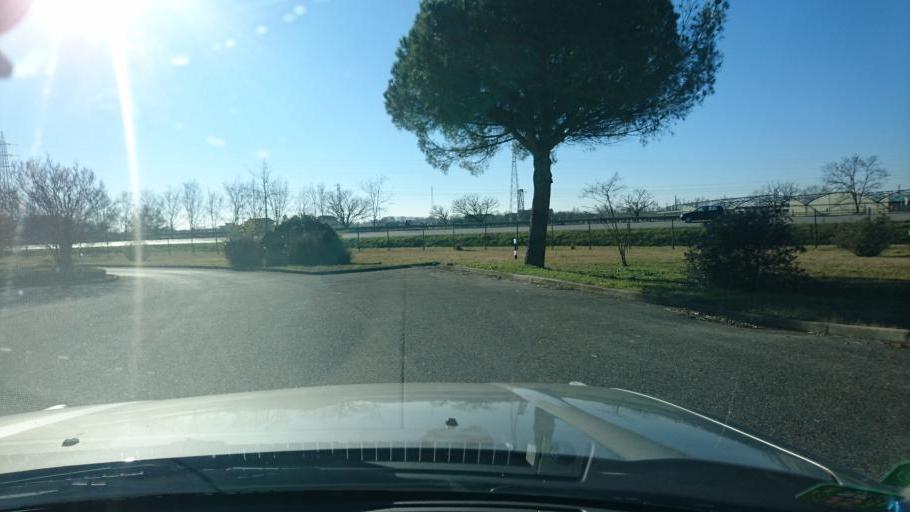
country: IT
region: Veneto
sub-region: Provincia di Rovigo
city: Porto Tolle
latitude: 44.9436
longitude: 12.3224
